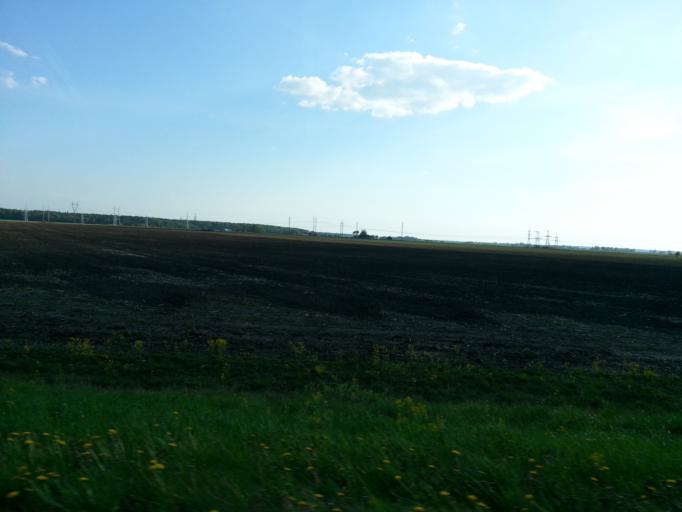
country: LT
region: Panevezys
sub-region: Panevezys City
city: Panevezys
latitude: 55.6830
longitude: 24.2916
